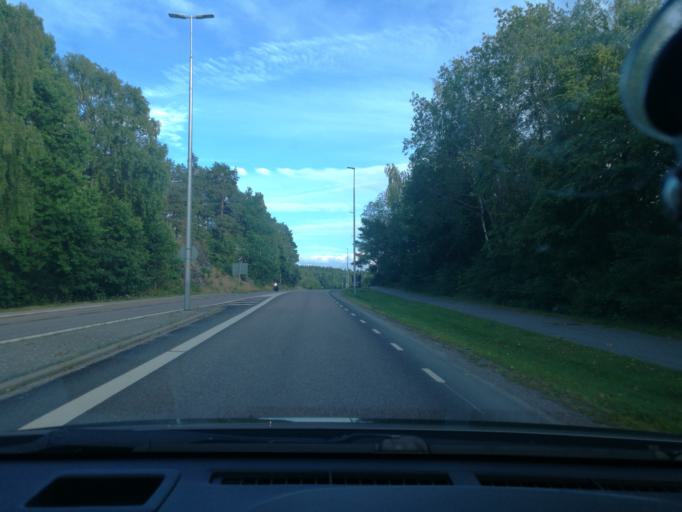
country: SE
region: Vaestmanland
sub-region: Vasteras
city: Vasteras
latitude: 59.6402
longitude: 16.5074
